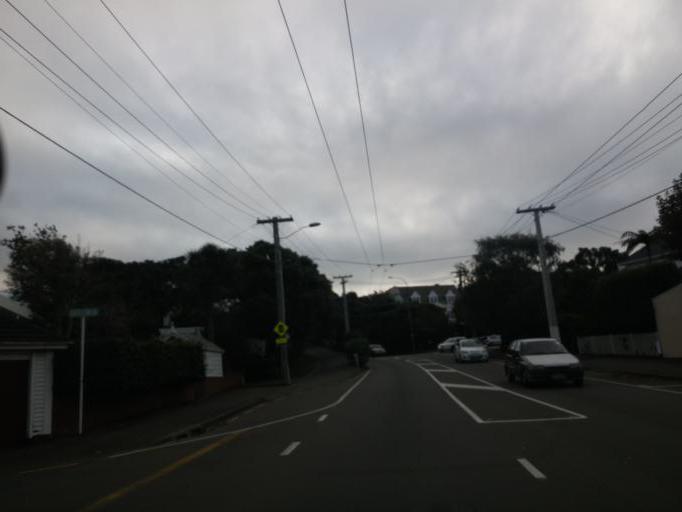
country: NZ
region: Wellington
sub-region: Wellington City
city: Kelburn
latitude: -41.2819
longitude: 174.7487
